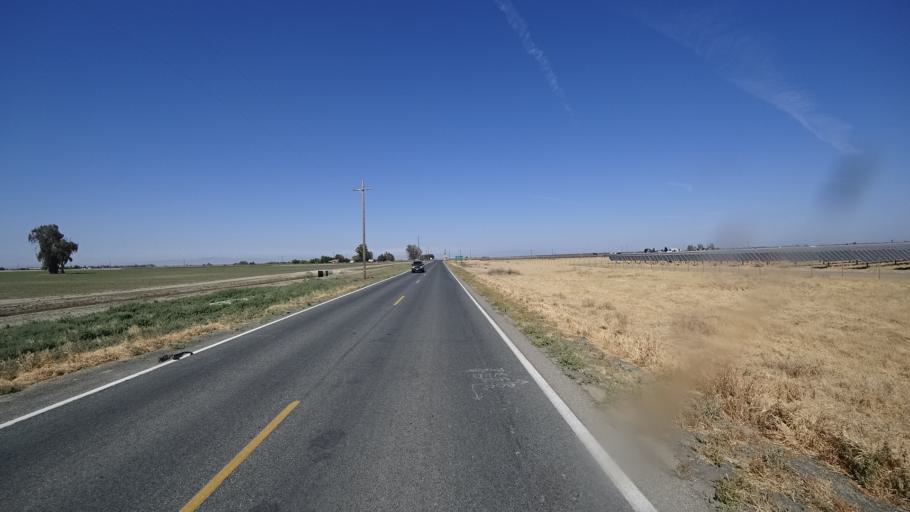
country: US
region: California
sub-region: Kings County
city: Stratford
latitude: 36.2115
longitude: -119.8115
